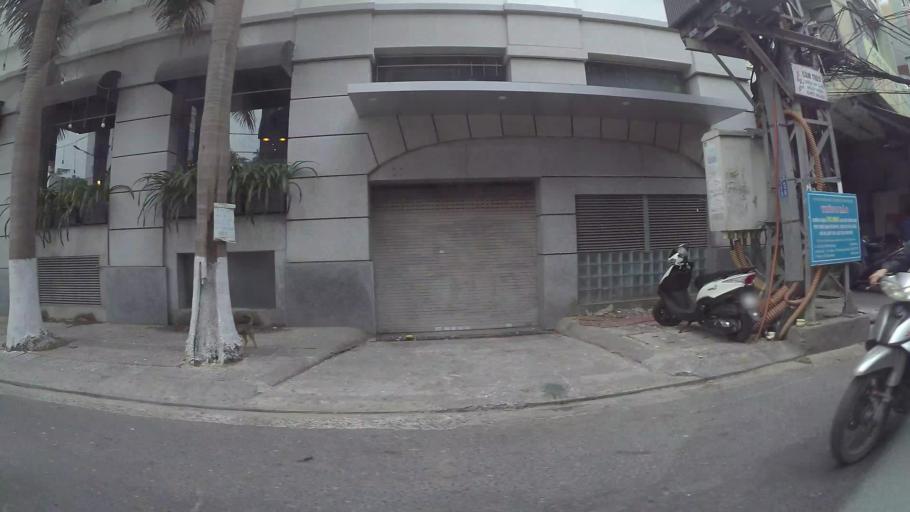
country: VN
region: Da Nang
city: Da Nang
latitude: 16.0606
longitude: 108.2137
